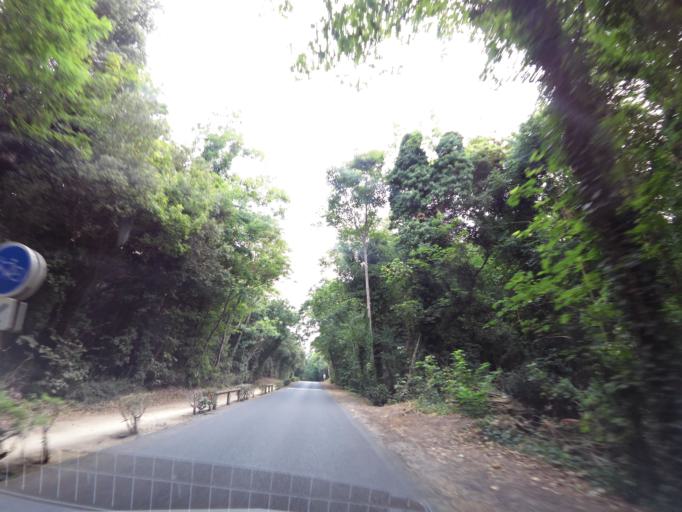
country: FR
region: Pays de la Loire
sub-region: Departement de la Vendee
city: Longeville-sur-Mer
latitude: 46.4026
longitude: -1.5026
